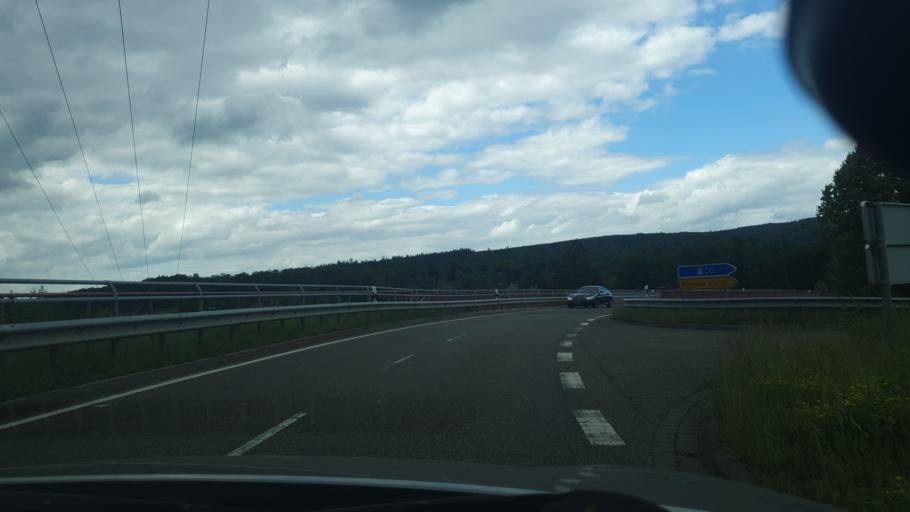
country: DE
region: Rheinland-Pfalz
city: Neuhausel
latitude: 50.3900
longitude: 7.7089
